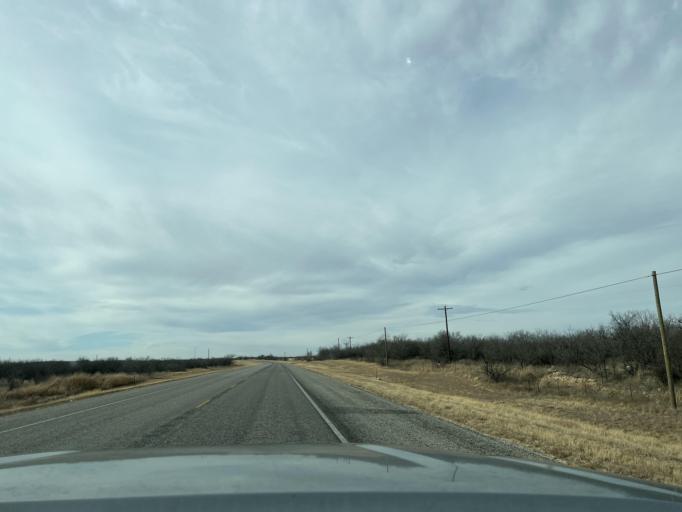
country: US
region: Texas
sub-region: Shackelford County
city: Albany
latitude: 32.7627
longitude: -99.5755
